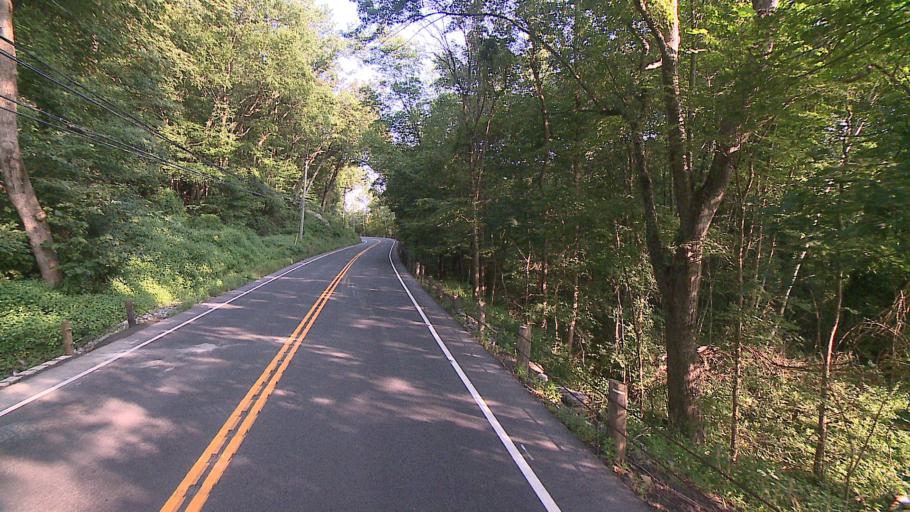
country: US
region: Connecticut
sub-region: Fairfield County
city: Sherman
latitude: 41.6306
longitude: -73.4702
